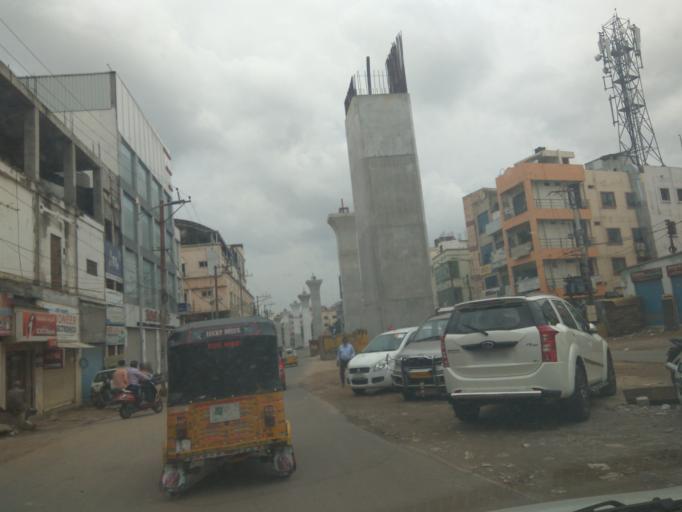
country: IN
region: Telangana
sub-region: Hyderabad
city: Malkajgiri
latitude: 17.4170
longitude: 78.4991
